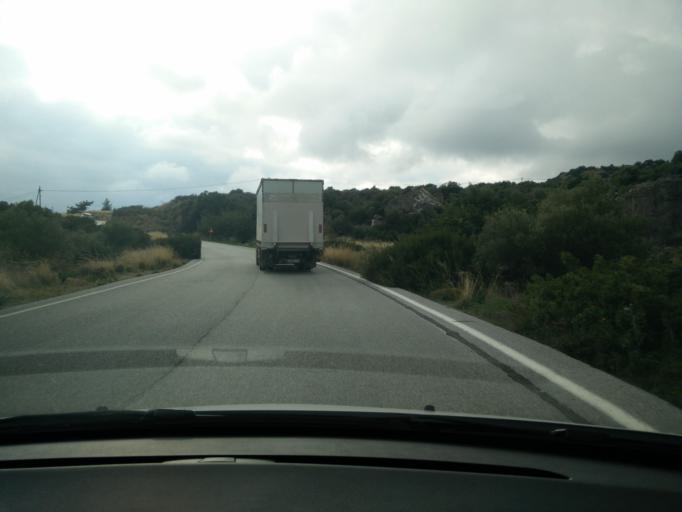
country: GR
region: Crete
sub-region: Nomos Lasithiou
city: Gra Liyia
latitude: 35.0218
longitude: 25.5532
